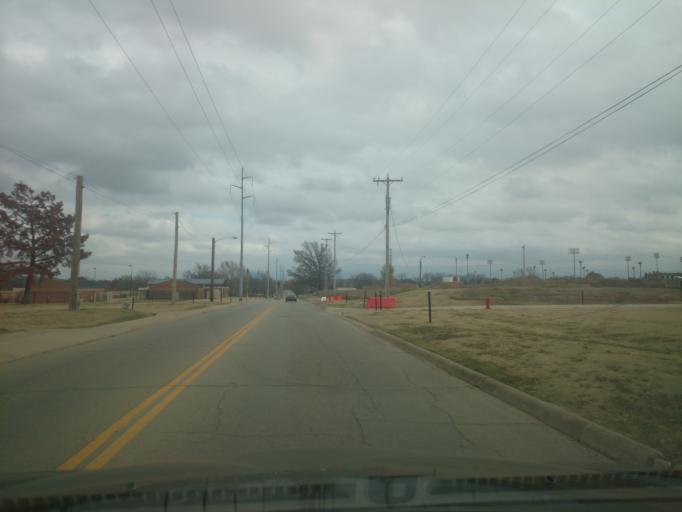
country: US
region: Oklahoma
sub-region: Payne County
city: Stillwater
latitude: 36.1305
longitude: -97.0681
